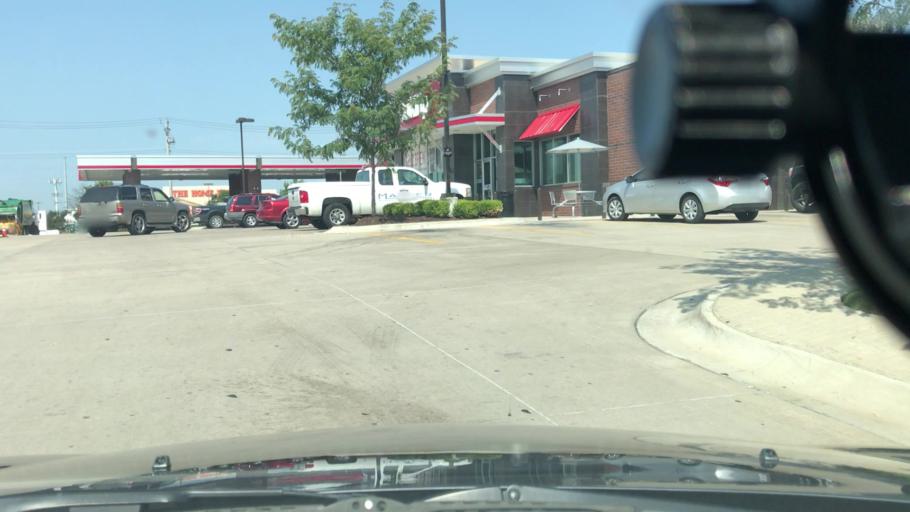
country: US
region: Missouri
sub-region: Saint Louis County
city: Richmond Heights
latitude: 38.6256
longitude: -90.3337
